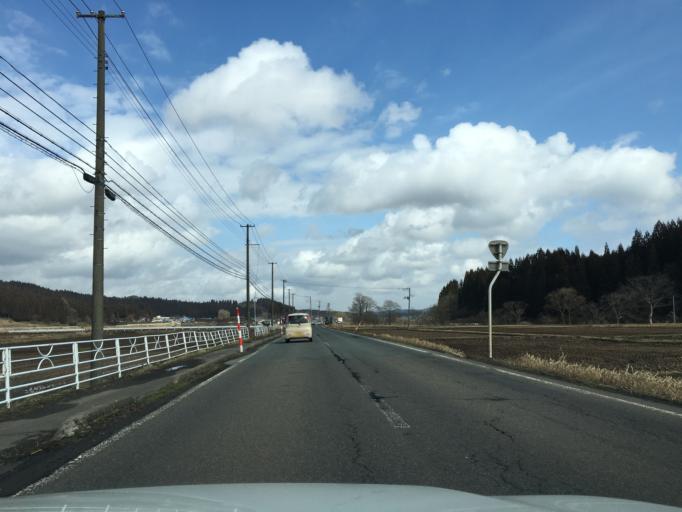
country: JP
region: Akita
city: Takanosu
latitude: 40.0364
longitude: 140.2768
